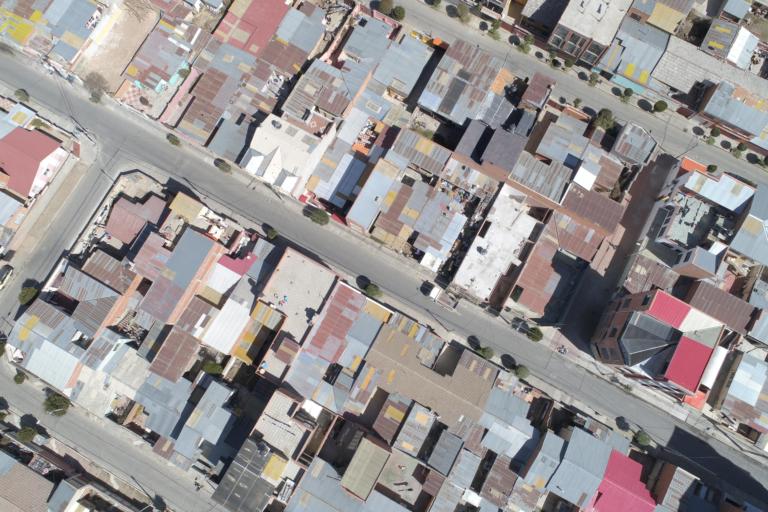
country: BO
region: La Paz
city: La Paz
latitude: -16.5279
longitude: -68.1556
